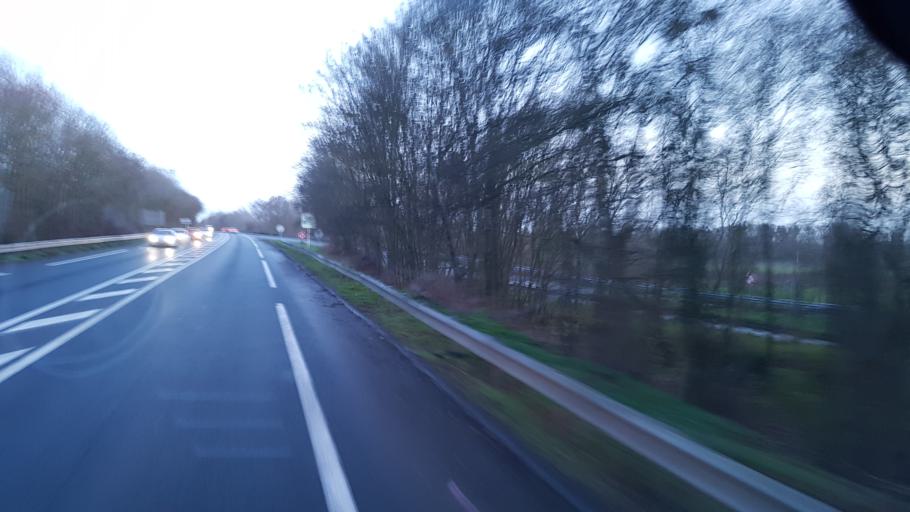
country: FR
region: Nord-Pas-de-Calais
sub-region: Departement du Nord
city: Courchelettes
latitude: 50.3562
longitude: 3.0481
